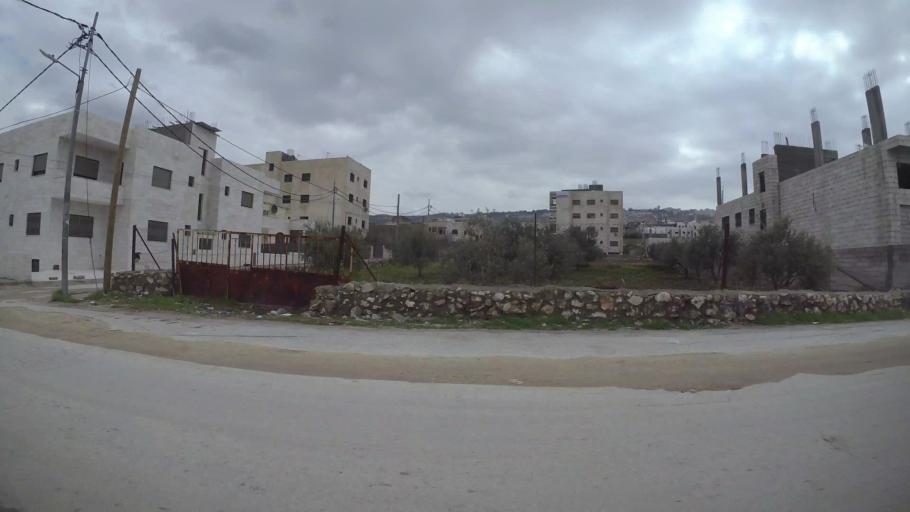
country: JO
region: Amman
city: Al Jubayhah
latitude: 32.0543
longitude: 35.8420
